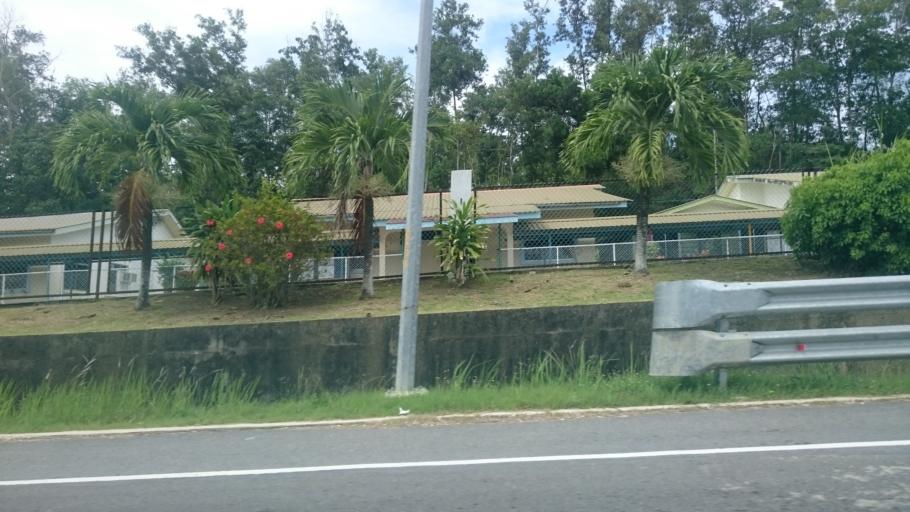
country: BN
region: Brunei and Muara
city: Bandar Seri Begawan
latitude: 4.8819
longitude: 114.8910
